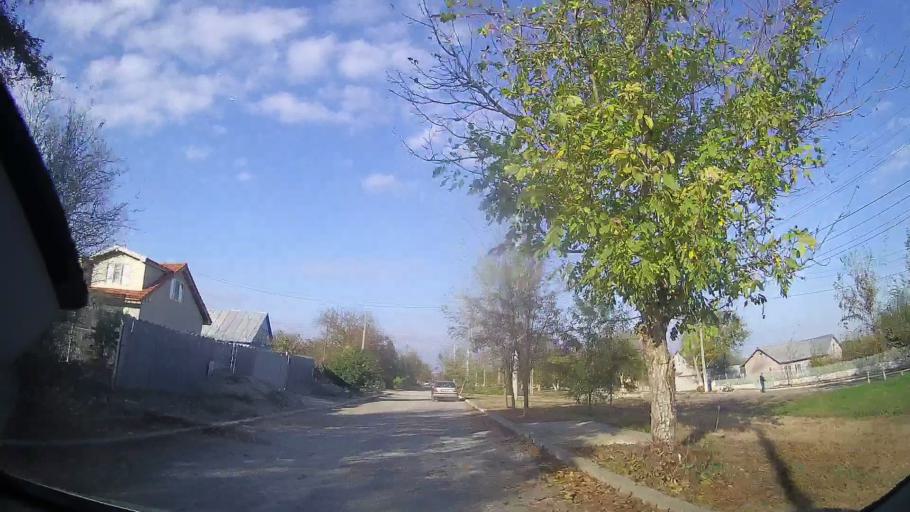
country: RO
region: Constanta
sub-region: Comuna Limanu
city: Limanu
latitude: 43.7961
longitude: 28.5300
